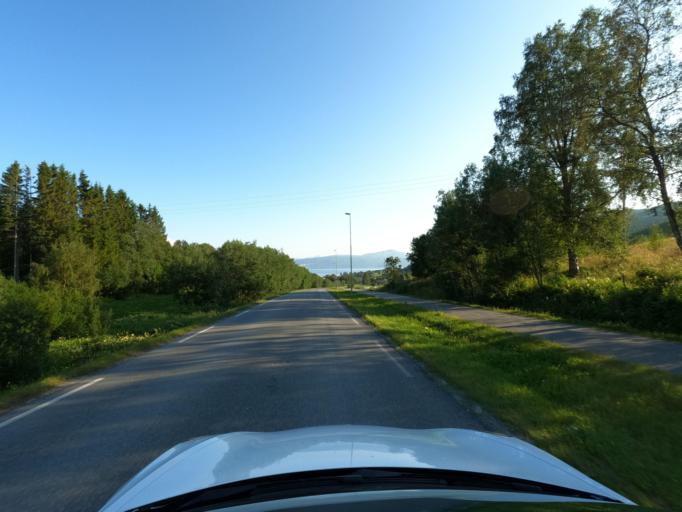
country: NO
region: Nordland
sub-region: Evenes
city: Randa
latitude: 68.4865
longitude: 16.8974
